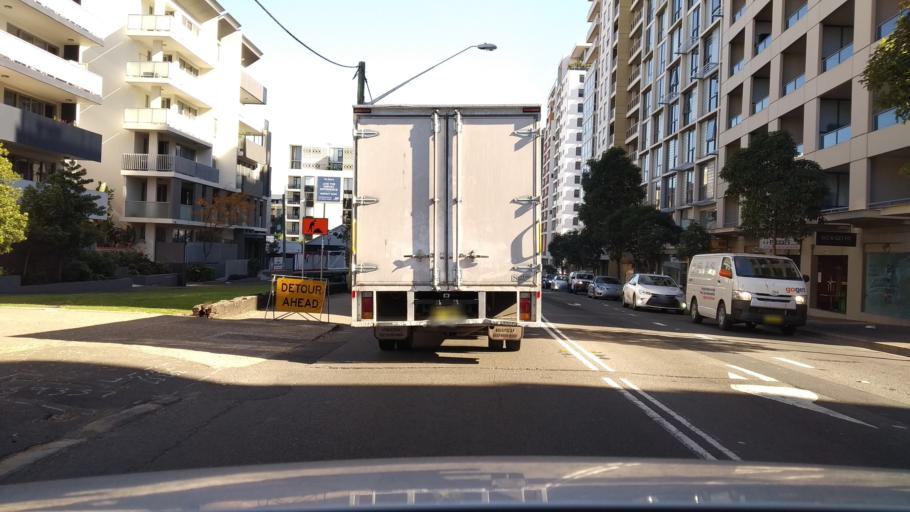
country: AU
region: New South Wales
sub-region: City of Sydney
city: Redfern
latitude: -33.9008
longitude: 151.2145
